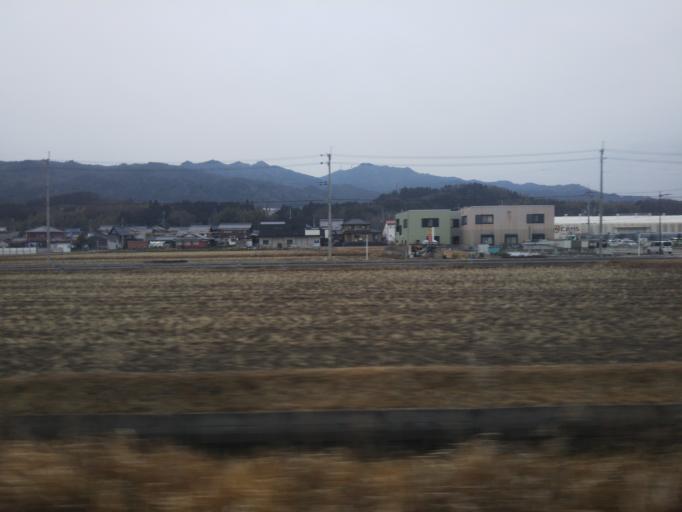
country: JP
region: Shiga Prefecture
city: Minakuchicho-matoba
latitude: 34.9960
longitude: 136.0902
